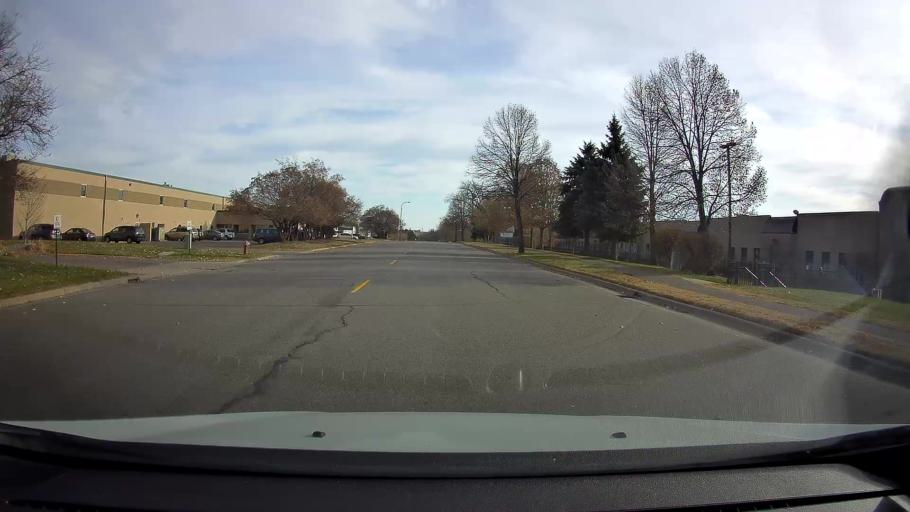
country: US
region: Minnesota
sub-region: Ramsey County
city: Lauderdale
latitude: 44.9825
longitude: -93.2155
